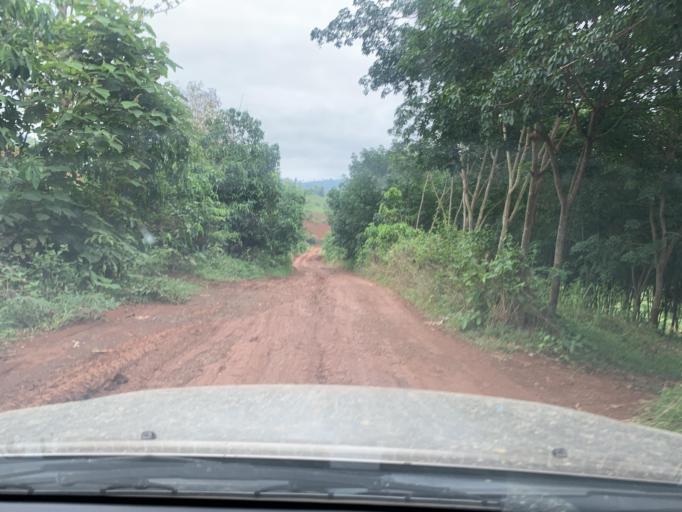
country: TH
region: Nan
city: Mae Charim
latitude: 18.4096
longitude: 101.4410
